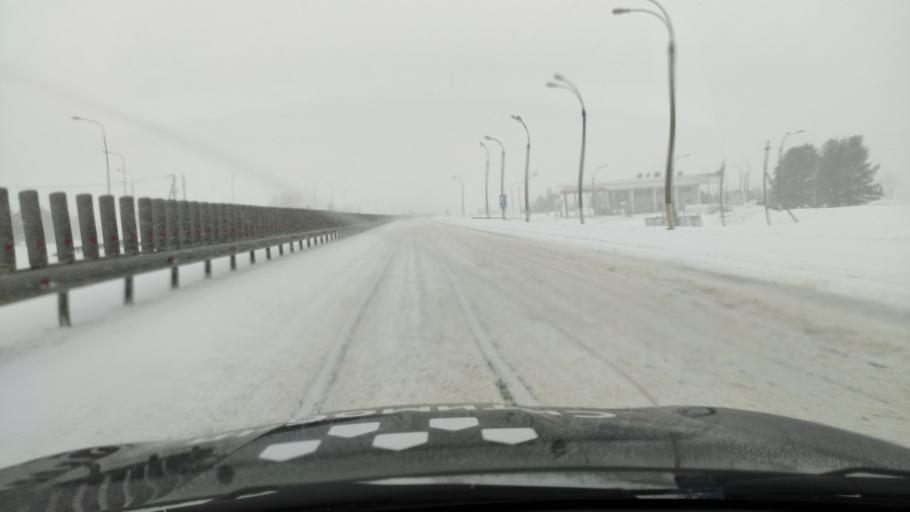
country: RU
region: Samara
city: Kurumoch
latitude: 53.4970
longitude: 50.0649
